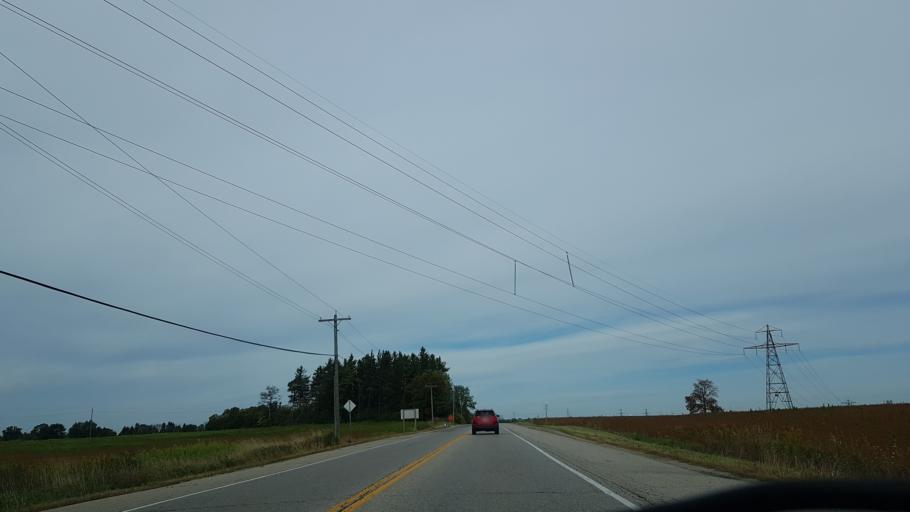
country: CA
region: Ontario
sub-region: Wellington County
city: Guelph
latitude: 43.5087
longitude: -80.2660
